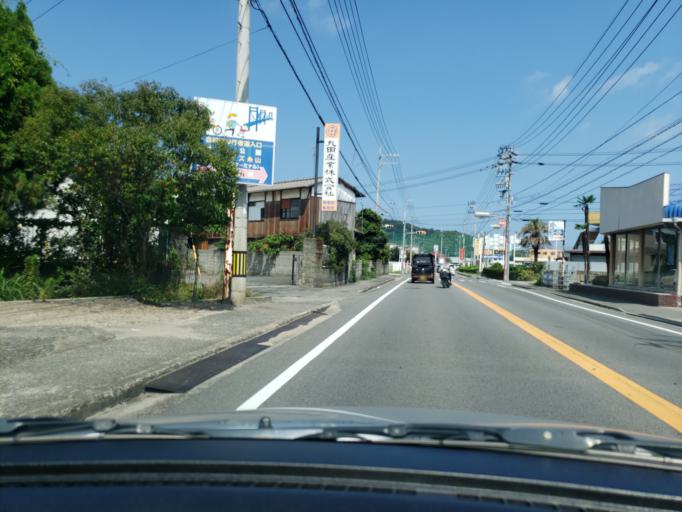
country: JP
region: Ehime
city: Hojo
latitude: 34.0995
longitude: 132.9699
